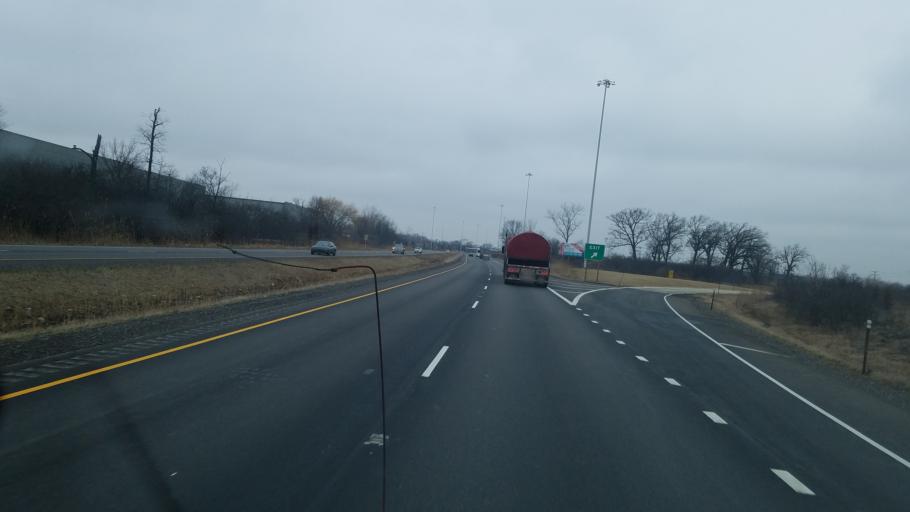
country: US
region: Illinois
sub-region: Lake County
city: Park City
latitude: 42.3414
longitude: -87.8875
